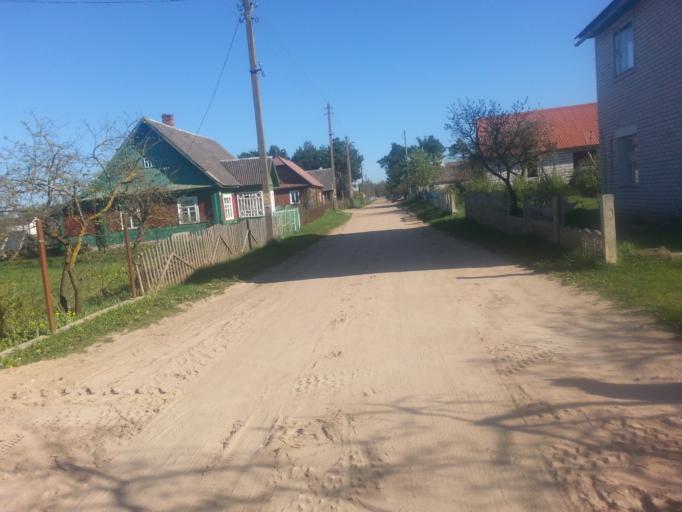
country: BY
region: Minsk
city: Narach
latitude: 54.9333
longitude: 26.6819
